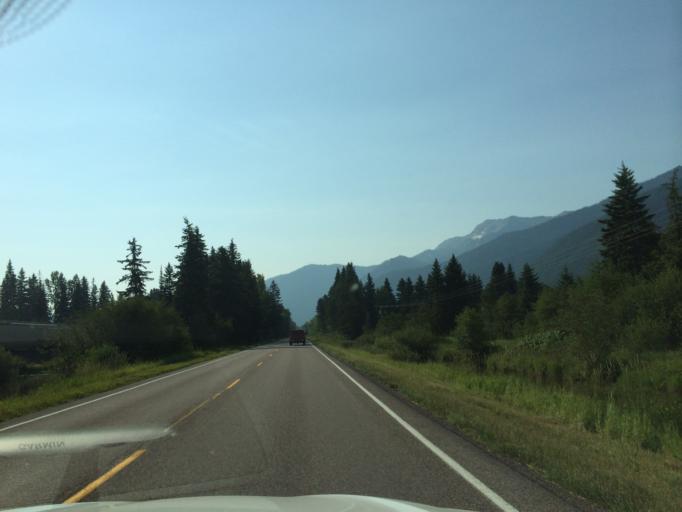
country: US
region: Montana
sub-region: Flathead County
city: Columbia Falls
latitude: 48.4610
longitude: -113.8282
